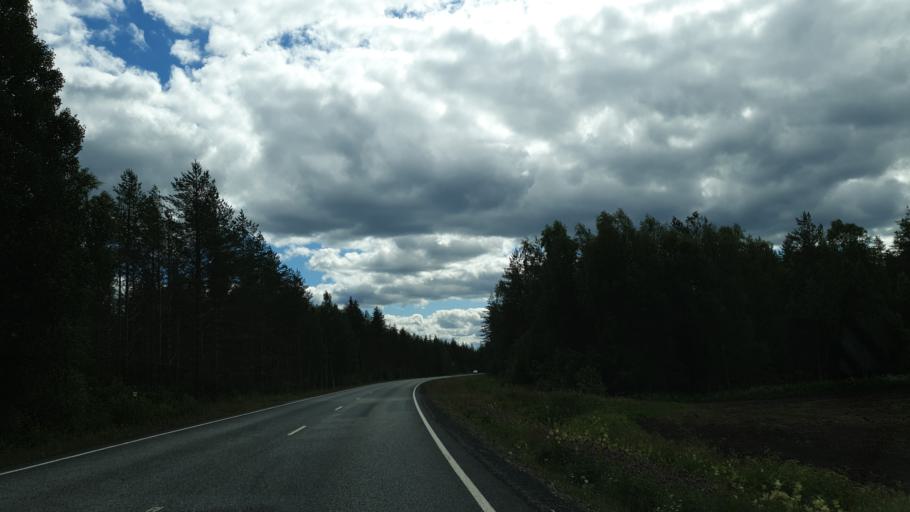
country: FI
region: Kainuu
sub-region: Kehys-Kainuu
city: Kuhmo
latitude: 64.0637
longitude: 29.5298
